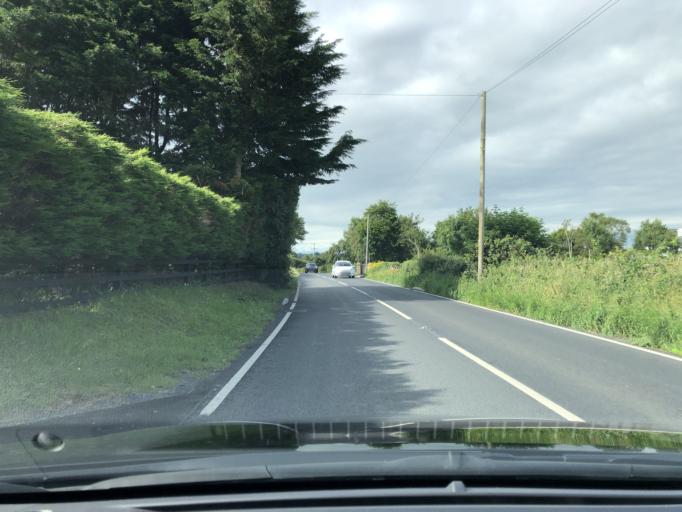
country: GB
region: Northern Ireland
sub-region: Down District
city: Dundrum
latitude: 54.2837
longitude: -5.8112
